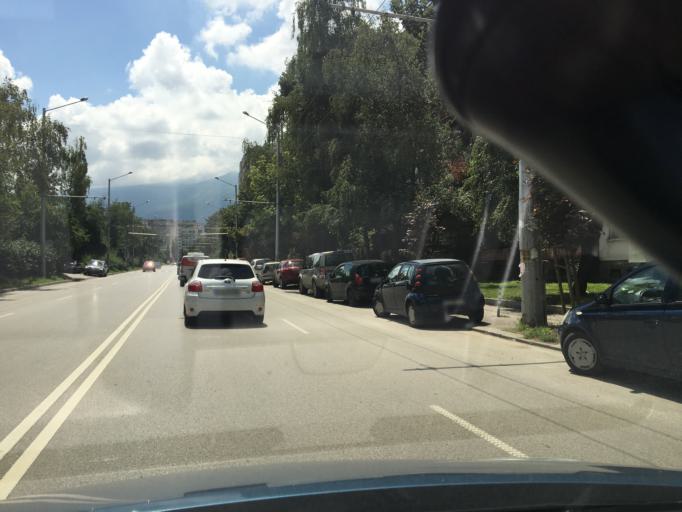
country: BG
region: Sofia-Capital
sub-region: Stolichna Obshtina
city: Sofia
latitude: 42.6684
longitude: 23.3035
